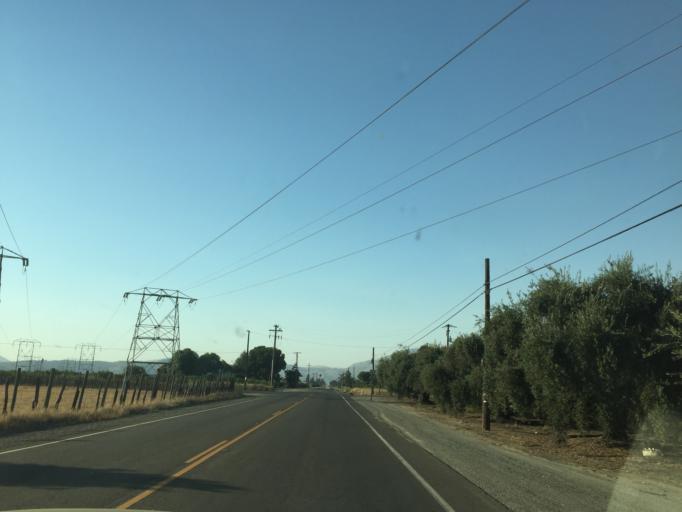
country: US
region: California
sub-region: Fresno County
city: Orange Cove
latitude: 36.6307
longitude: -119.3048
